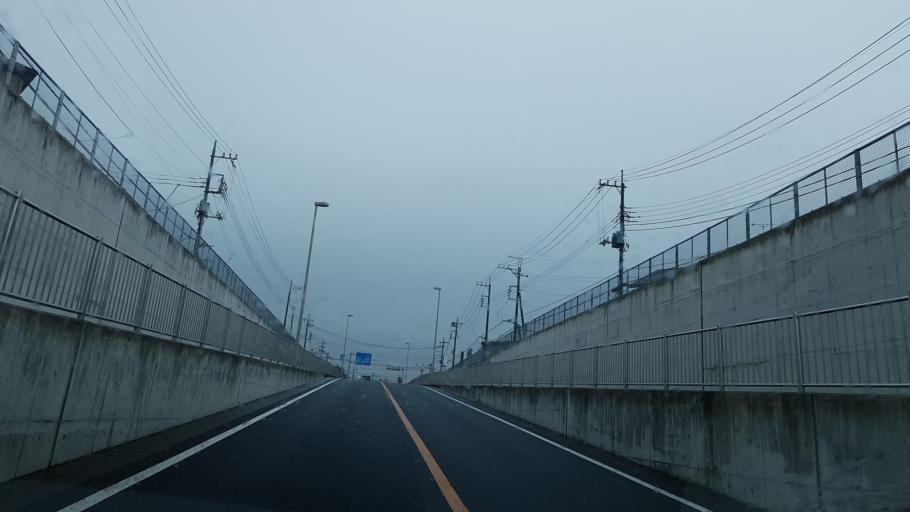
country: JP
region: Tochigi
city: Utsunomiya-shi
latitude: 36.5811
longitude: 139.9199
